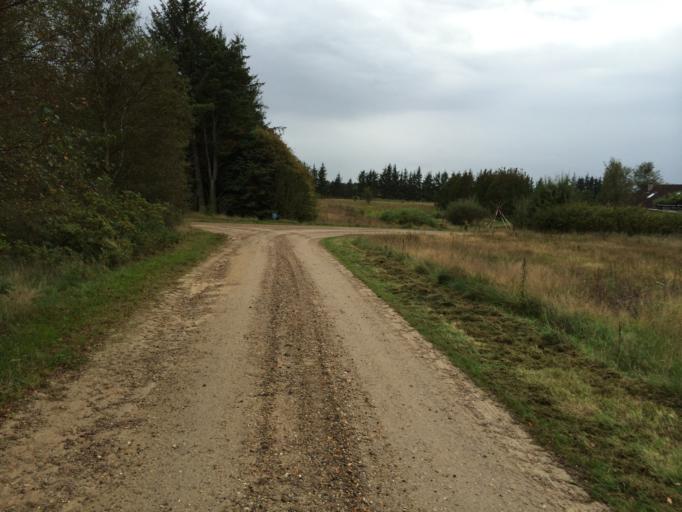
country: DK
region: Central Jutland
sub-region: Holstebro Kommune
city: Ulfborg
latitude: 56.2492
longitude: 8.4213
